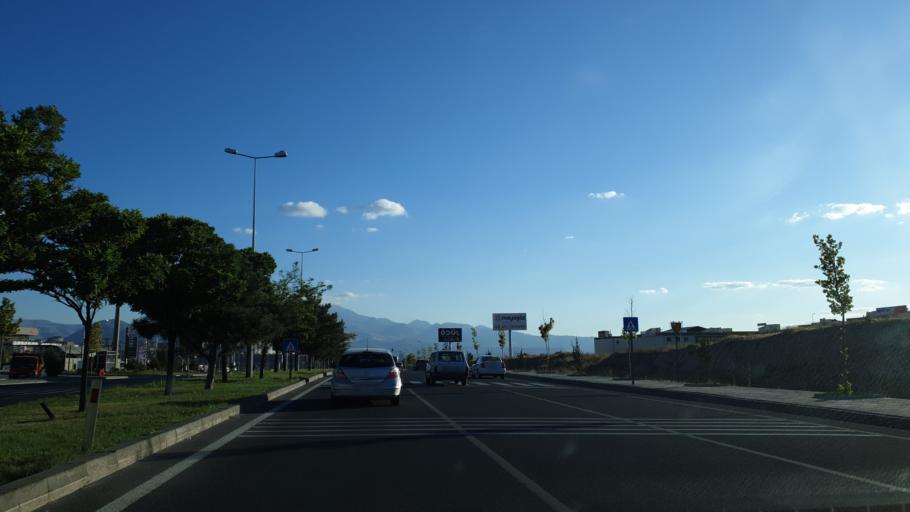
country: TR
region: Kayseri
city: Kocasinan
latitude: 38.7789
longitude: 35.5750
